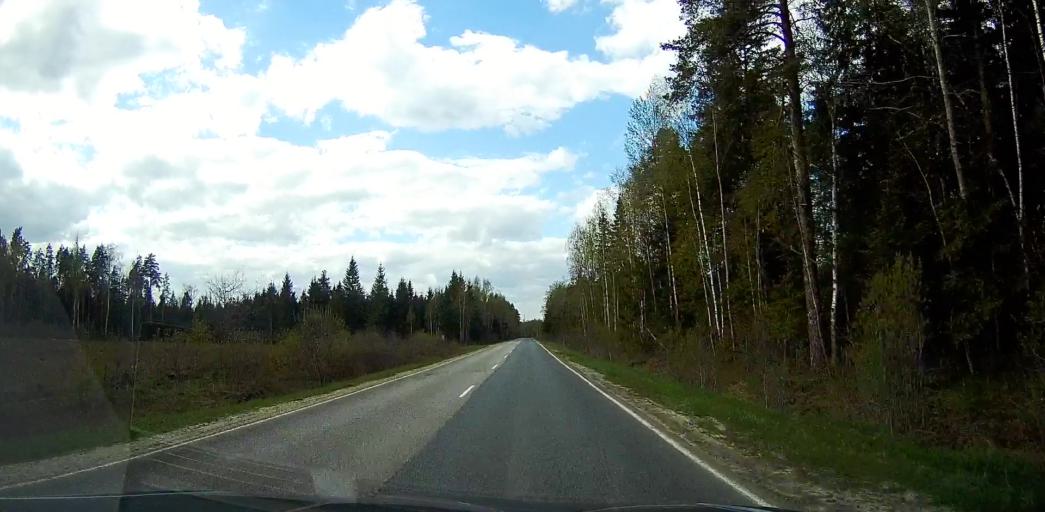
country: RU
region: Moskovskaya
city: Rakhmanovo
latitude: 55.6487
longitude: 38.6667
